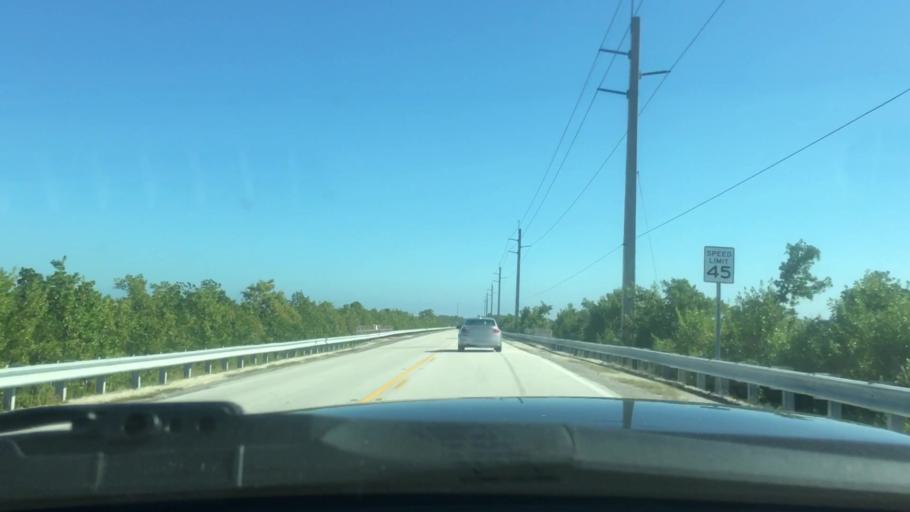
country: US
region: Florida
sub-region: Monroe County
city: North Key Largo
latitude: 25.2845
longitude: -80.3103
